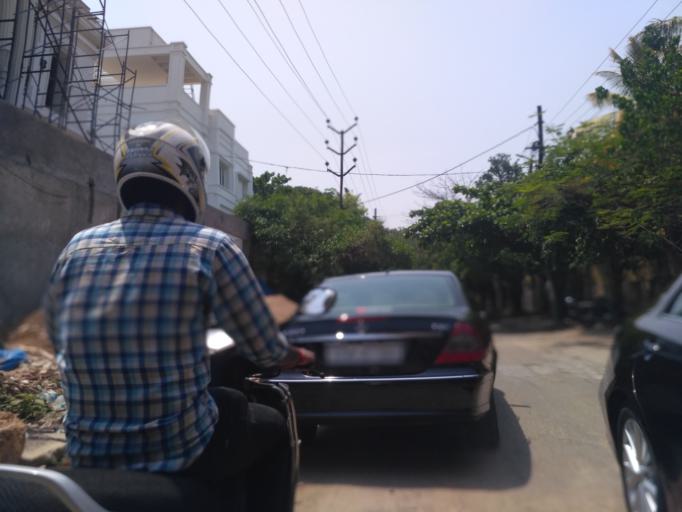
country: IN
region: Telangana
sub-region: Rangareddi
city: Kukatpalli
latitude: 17.4276
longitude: 78.4075
